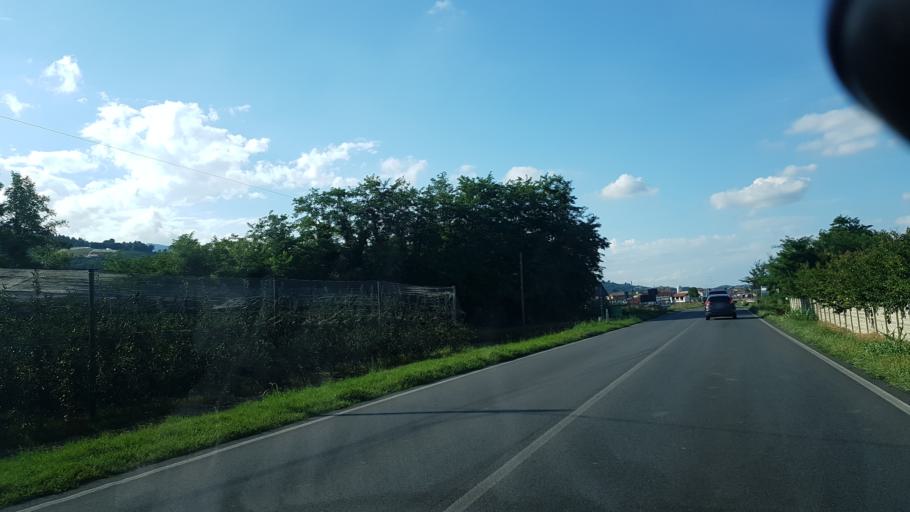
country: IT
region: Piedmont
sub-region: Provincia di Cuneo
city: Costiglione Saluzzo
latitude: 44.5515
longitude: 7.4915
